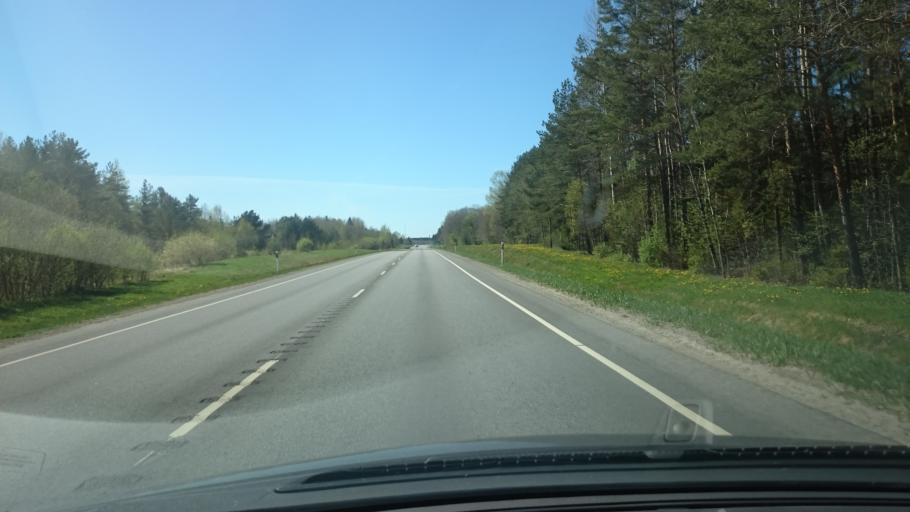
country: EE
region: Ida-Virumaa
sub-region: Johvi vald
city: Johvi
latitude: 59.3647
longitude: 27.4468
